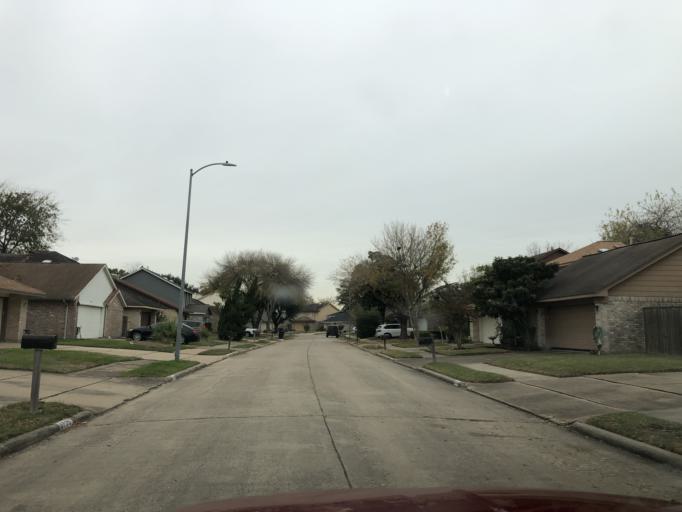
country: US
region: Texas
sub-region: Fort Bend County
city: Missouri City
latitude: 29.6416
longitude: -95.5313
